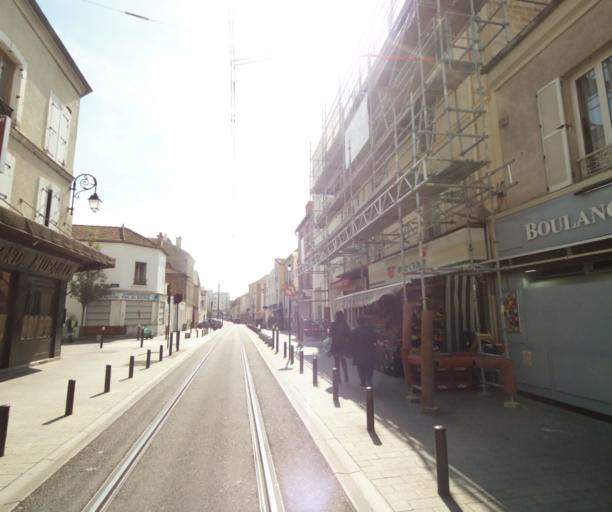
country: FR
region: Ile-de-France
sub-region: Departement des Hauts-de-Seine
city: Gennevilliers
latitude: 48.9327
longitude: 2.2975
